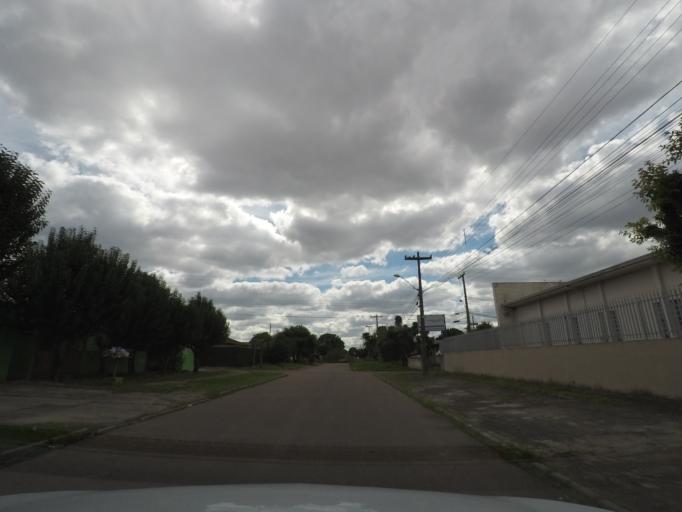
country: BR
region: Parana
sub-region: Sao Jose Dos Pinhais
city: Sao Jose dos Pinhais
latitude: -25.4846
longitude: -49.2375
